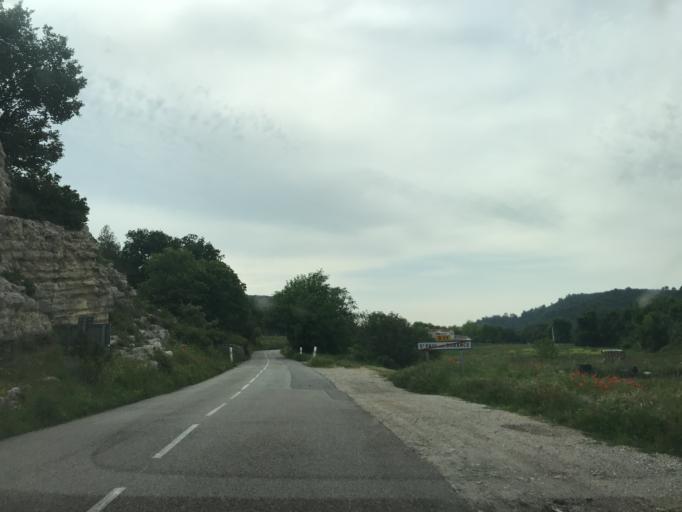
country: FR
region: Provence-Alpes-Cote d'Azur
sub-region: Departement du Vaucluse
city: Beaumont-de-Pertuis
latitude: 43.6847
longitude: 5.7118
